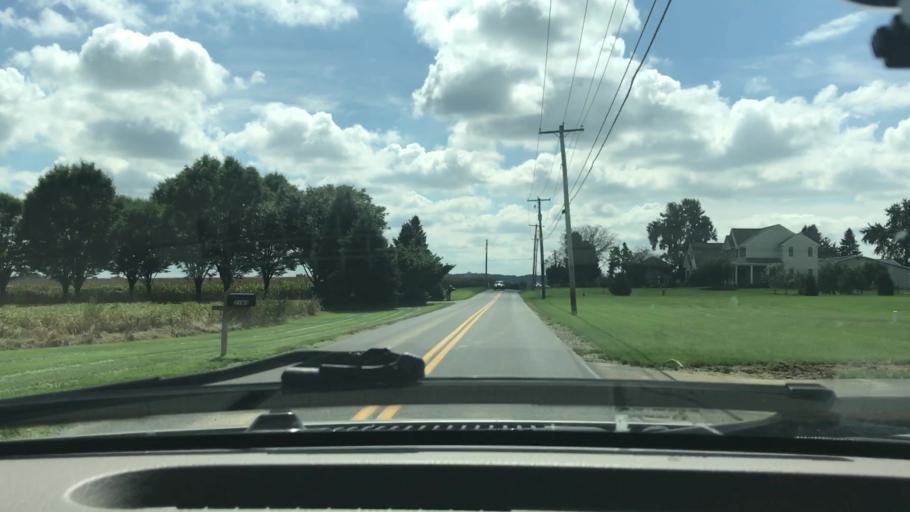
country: US
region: Pennsylvania
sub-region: Lancaster County
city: Landisville
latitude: 40.1120
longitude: -76.3861
